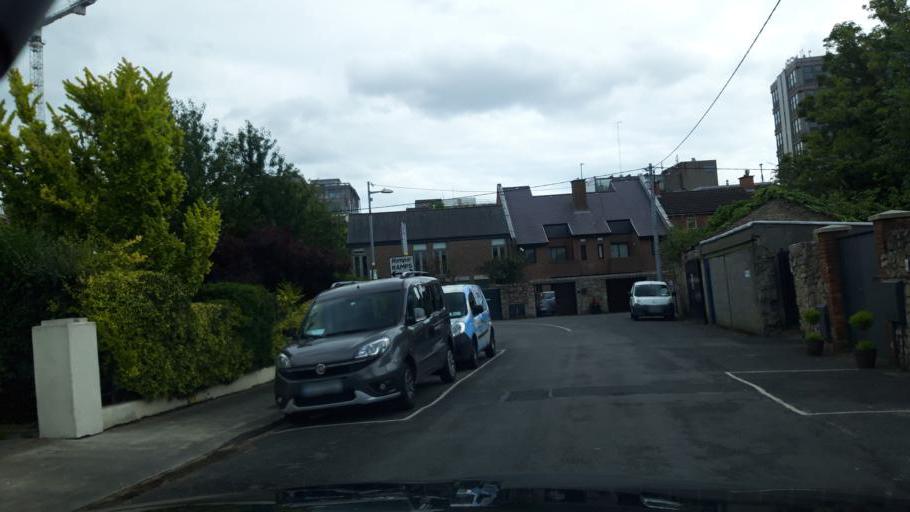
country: IE
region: Leinster
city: Ringsend
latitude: 53.3339
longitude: -6.2352
